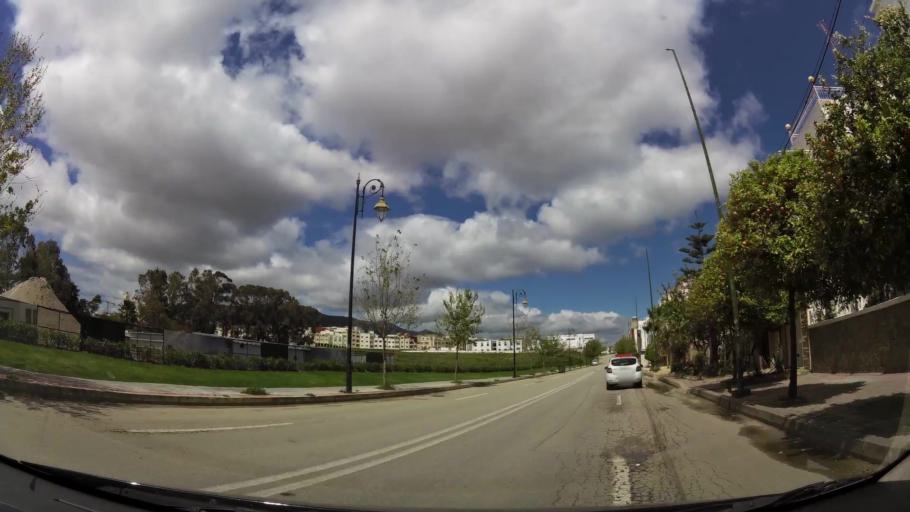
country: MA
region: Tanger-Tetouan
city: Tetouan
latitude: 35.5826
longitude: -5.3361
